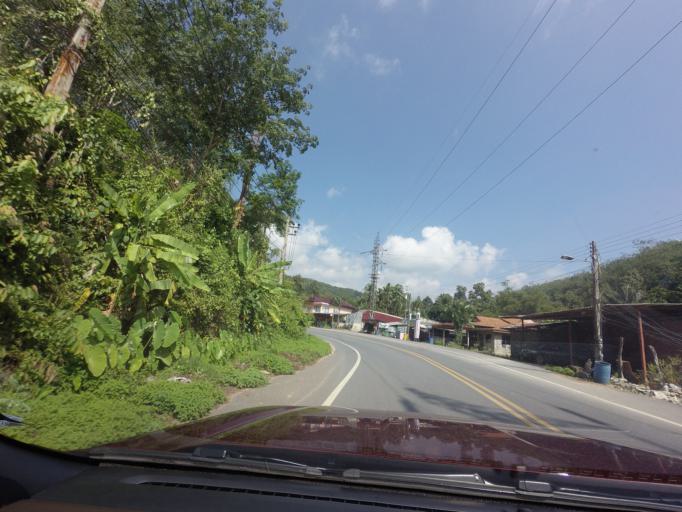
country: TH
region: Yala
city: Betong
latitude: 5.9176
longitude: 101.1733
